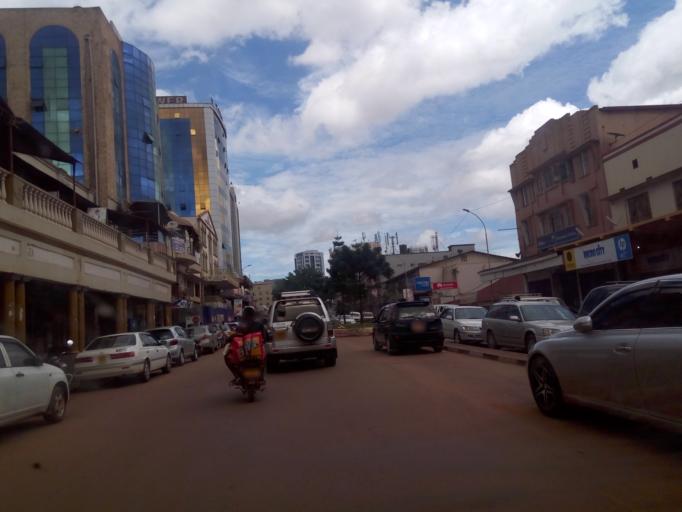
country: UG
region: Central Region
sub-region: Kampala District
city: Kampala
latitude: 0.3160
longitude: 32.5770
